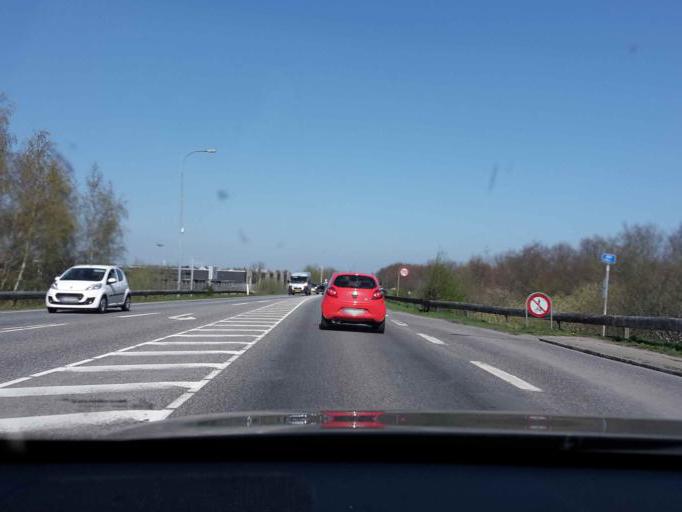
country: DK
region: South Denmark
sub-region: Odense Kommune
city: Bellinge
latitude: 55.3542
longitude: 10.3370
